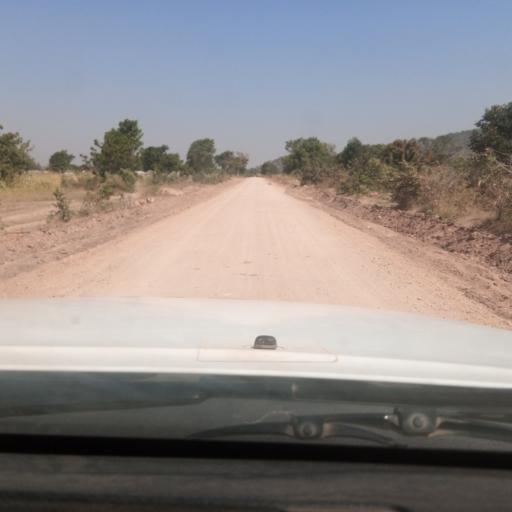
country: NG
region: Adamawa
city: Yola
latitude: 9.0601
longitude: 12.3867
